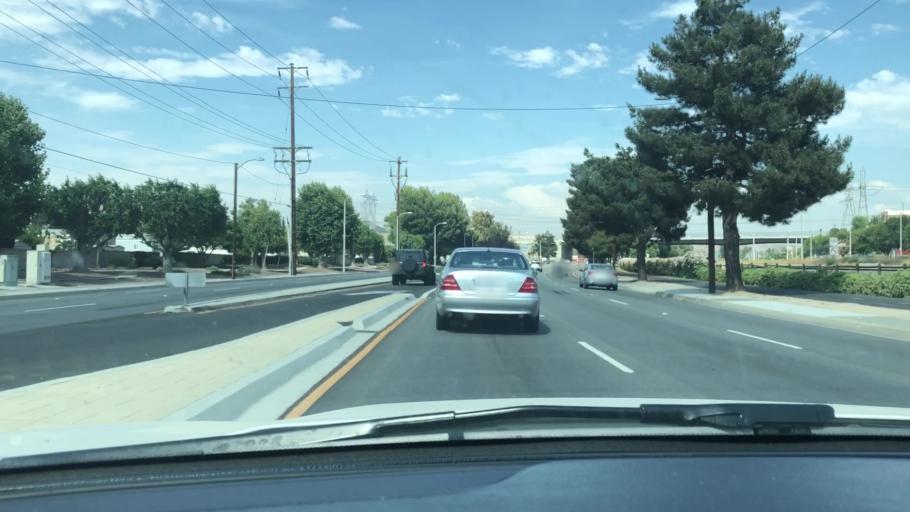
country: US
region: California
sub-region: Los Angeles County
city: Santa Clarita
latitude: 34.4192
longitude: -118.5071
